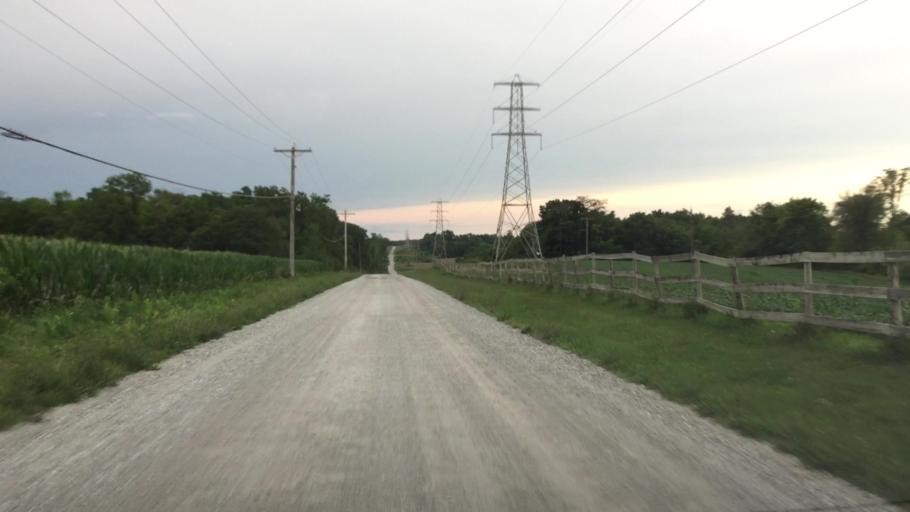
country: US
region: Illinois
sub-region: Hancock County
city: Hamilton
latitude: 40.3709
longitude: -91.3613
